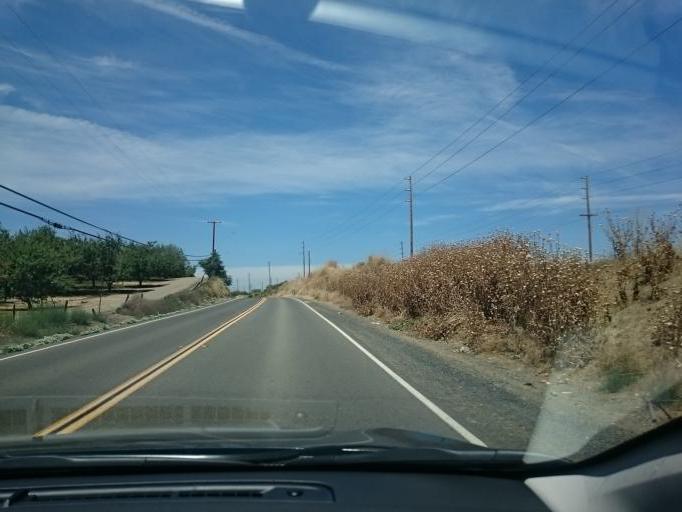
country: US
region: California
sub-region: Stanislaus County
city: Waterford
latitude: 37.6438
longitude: -120.6493
